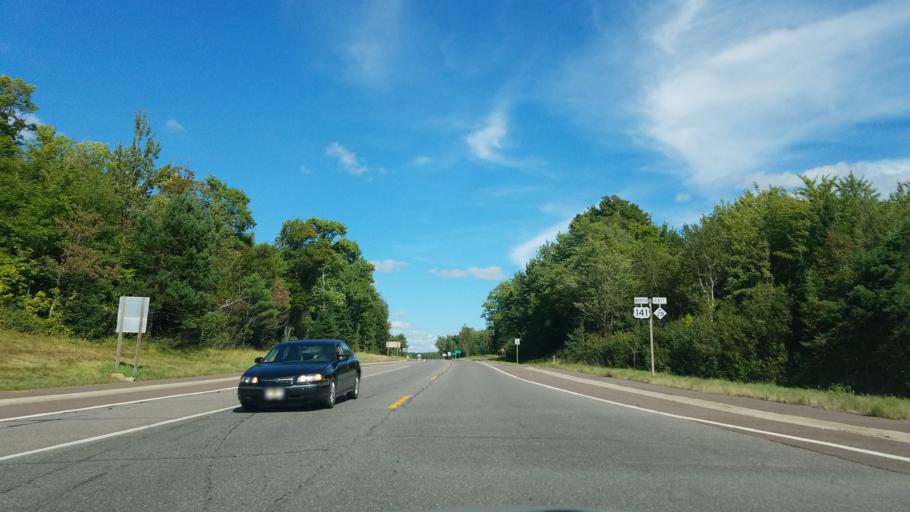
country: US
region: Michigan
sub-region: Baraga County
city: L'Anse
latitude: 46.5465
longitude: -88.5369
